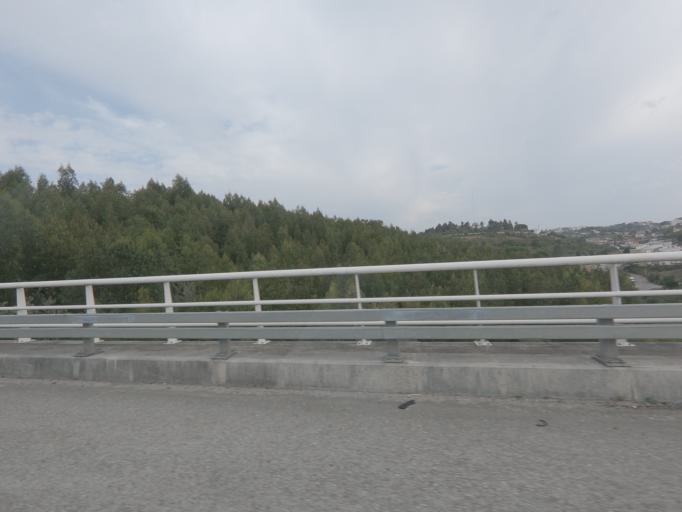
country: PT
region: Coimbra
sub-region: Coimbra
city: Coimbra
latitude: 40.2051
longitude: -8.4499
